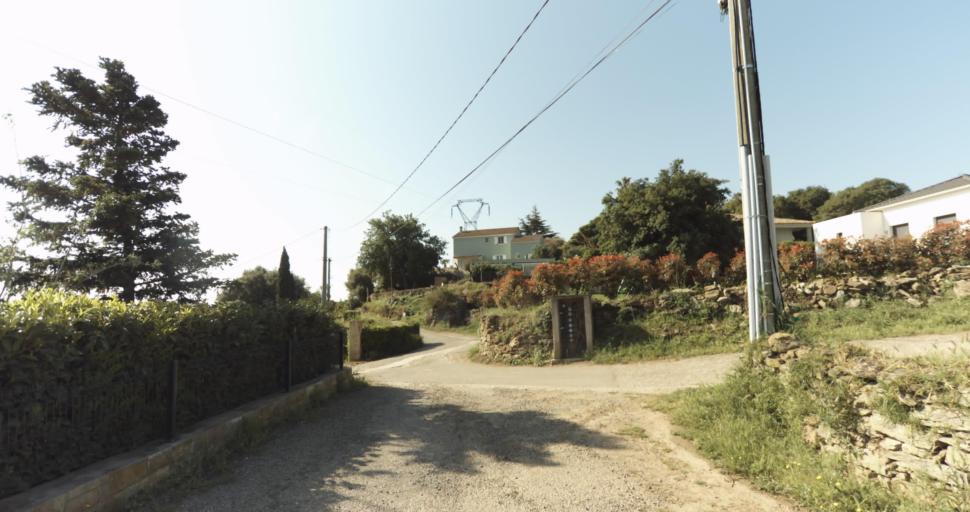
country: FR
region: Corsica
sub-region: Departement de la Haute-Corse
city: Biguglia
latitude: 42.6312
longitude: 9.4244
